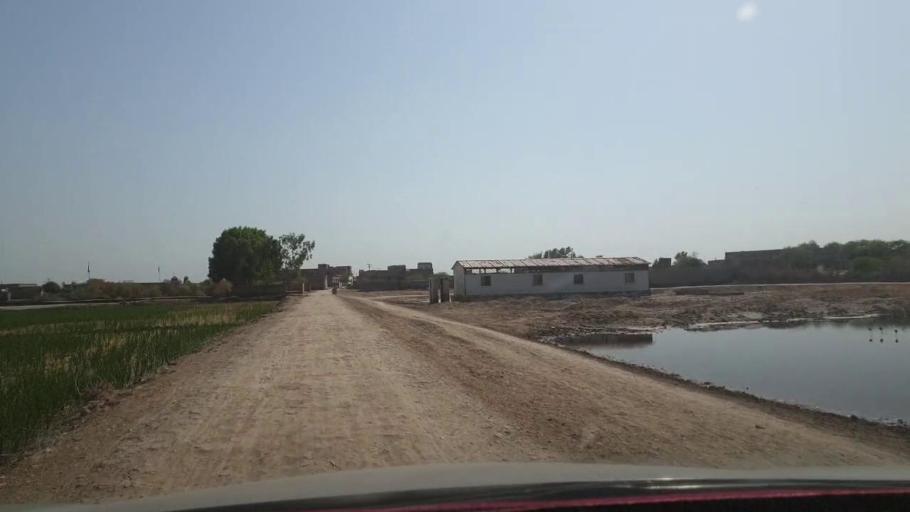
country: PK
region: Sindh
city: Nasirabad
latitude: 27.3475
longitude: 67.8416
